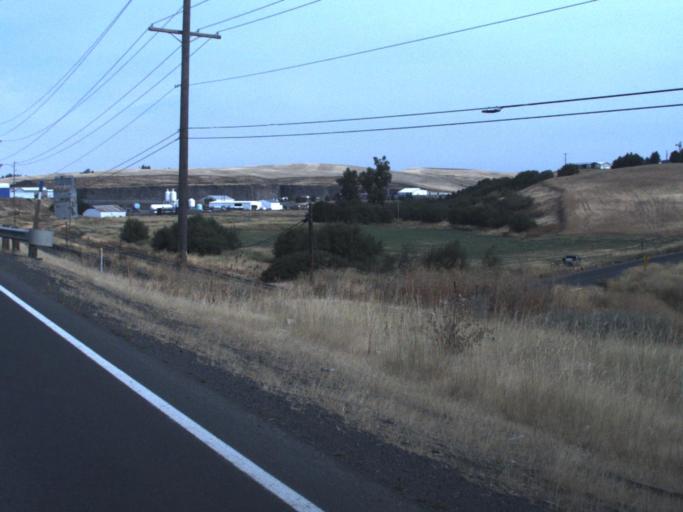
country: US
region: Washington
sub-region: Whitman County
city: Pullman
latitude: 46.7540
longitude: -117.1703
